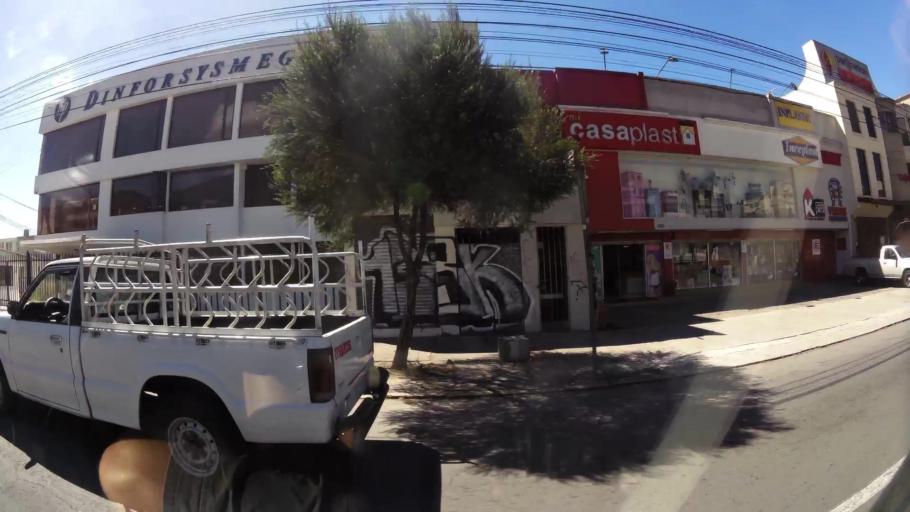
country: EC
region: Pichincha
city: Quito
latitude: -0.1825
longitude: -78.4948
